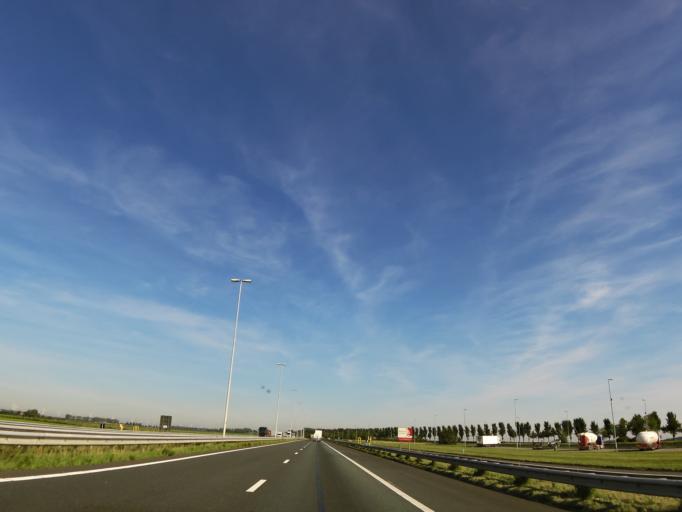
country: NL
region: North Brabant
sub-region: Gemeente Woensdrecht
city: Woensdrecht
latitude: 51.3783
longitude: 4.3035
